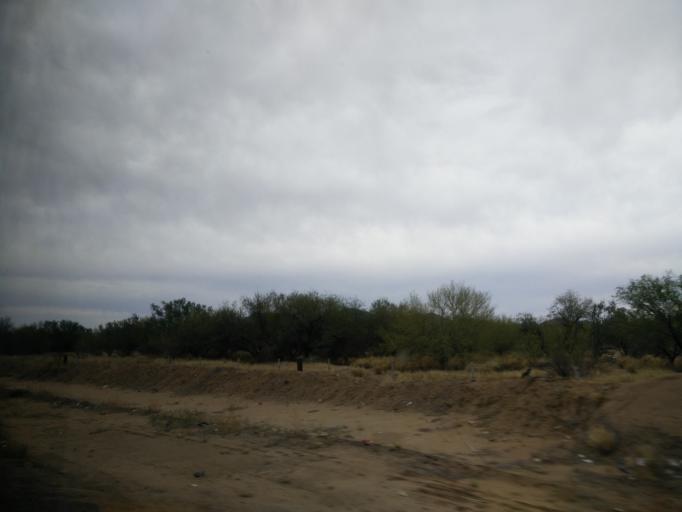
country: MX
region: Sonora
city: Hermosillo
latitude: 28.7606
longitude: -110.9699
